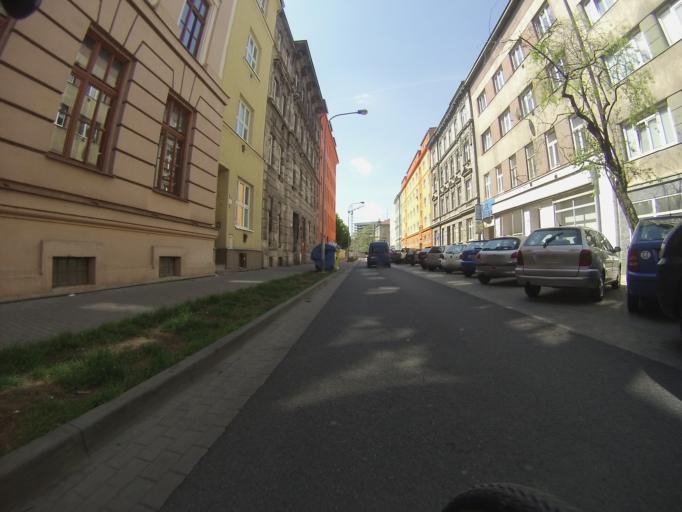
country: CZ
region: South Moravian
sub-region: Mesto Brno
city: Brno
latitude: 49.1912
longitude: 16.6197
